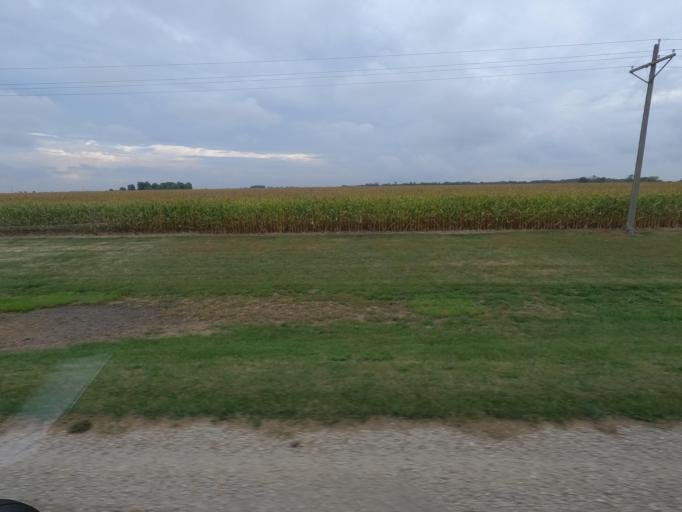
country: US
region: Iowa
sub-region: Van Buren County
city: Keosauqua
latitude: 40.8135
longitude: -91.8374
